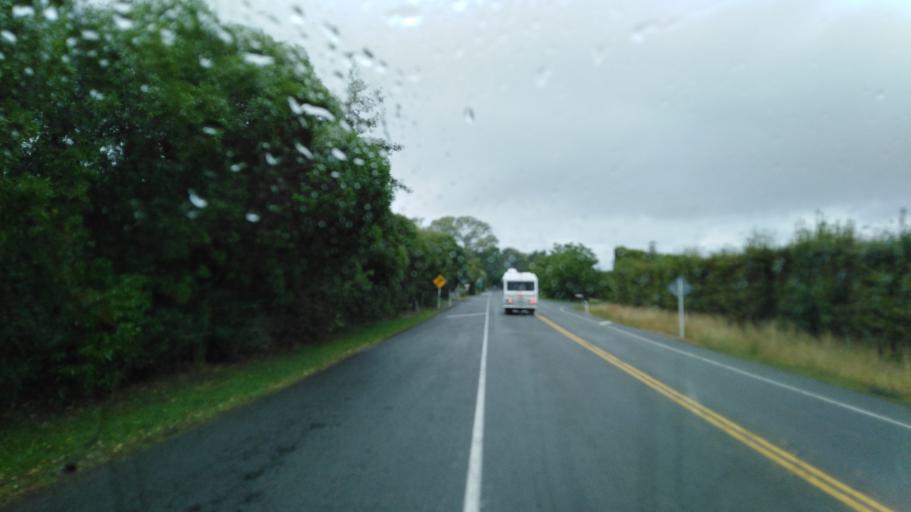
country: NZ
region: Marlborough
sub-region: Marlborough District
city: Blenheim
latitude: -41.4584
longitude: 173.9494
